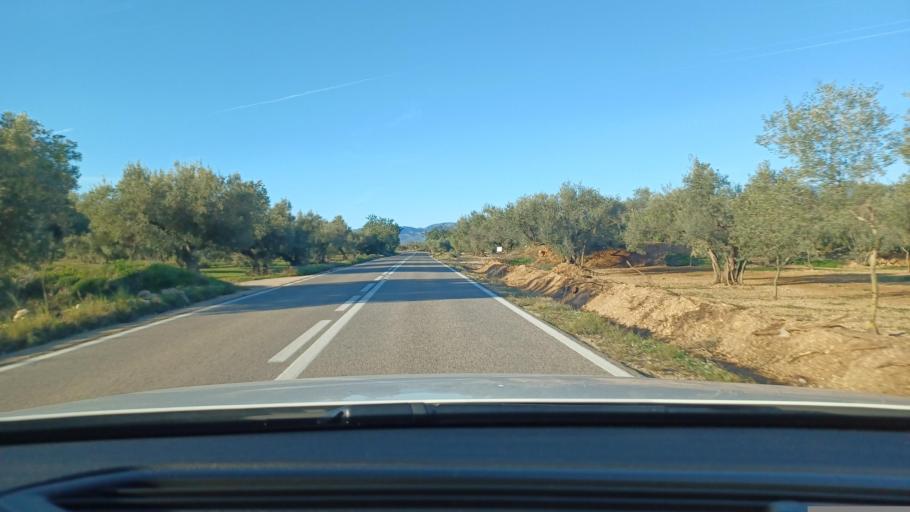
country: ES
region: Catalonia
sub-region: Provincia de Tarragona
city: Mas de Barberans
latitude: 40.7199
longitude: 0.4267
